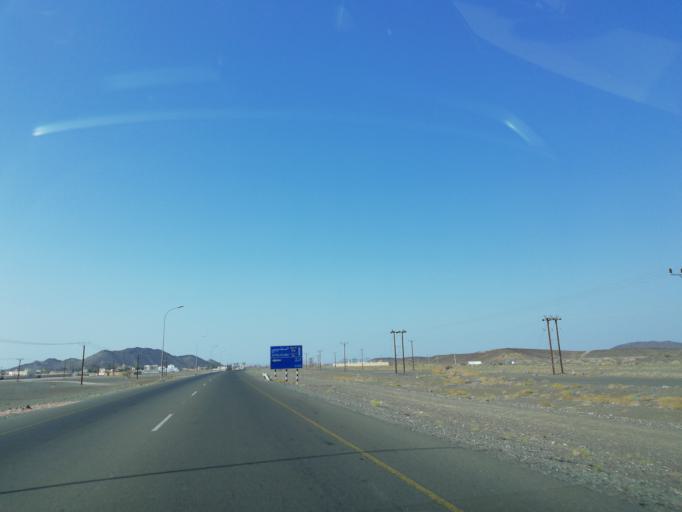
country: OM
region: Ash Sharqiyah
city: Ibra'
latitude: 22.7277
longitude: 58.1501
